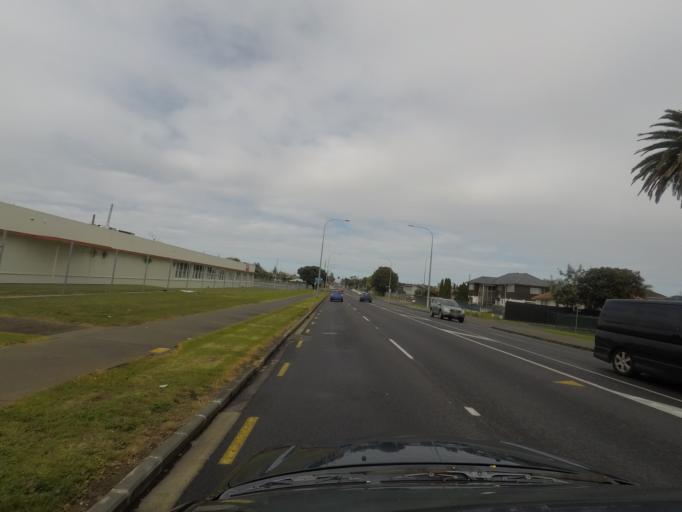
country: NZ
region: Auckland
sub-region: Auckland
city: Tamaki
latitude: -36.9014
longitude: 174.8431
